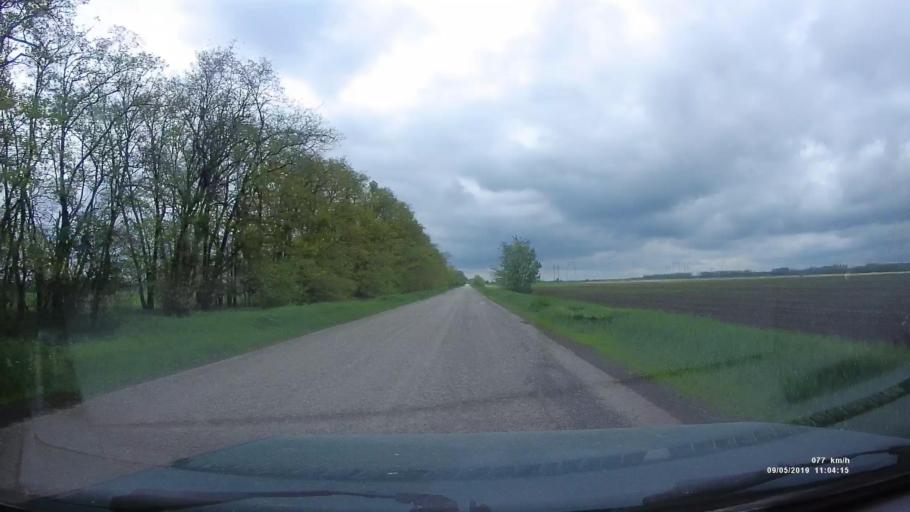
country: RU
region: Krasnodarskiy
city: Kanelovskaya
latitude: 46.8192
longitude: 39.2100
